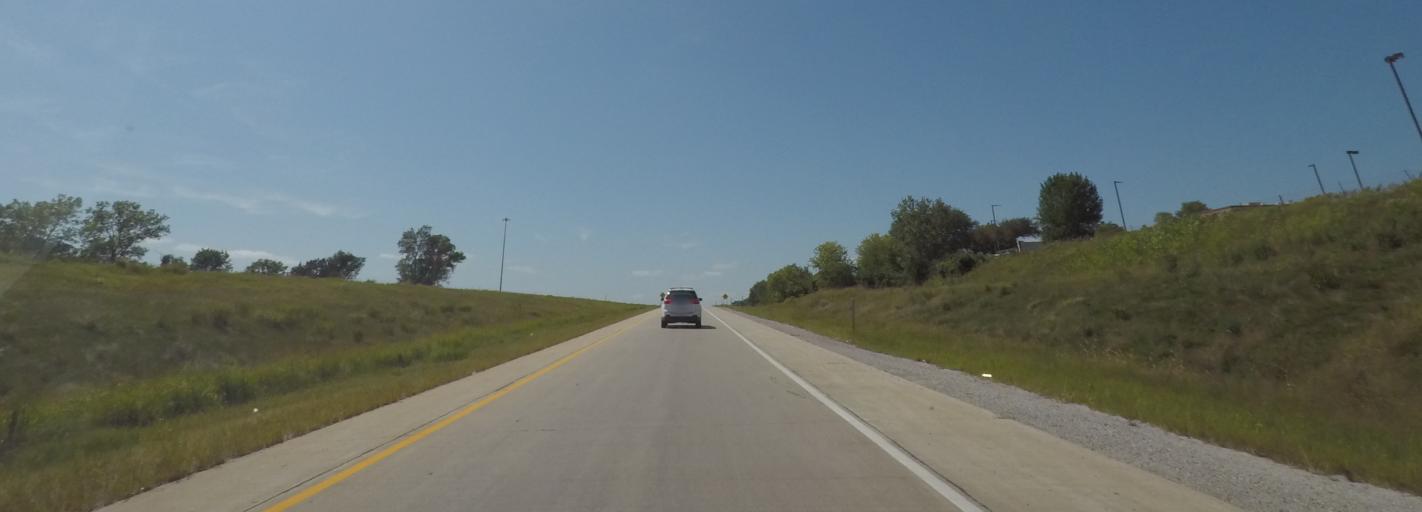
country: US
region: Iowa
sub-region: Johnson County
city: Coralville
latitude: 41.6947
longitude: -91.6105
